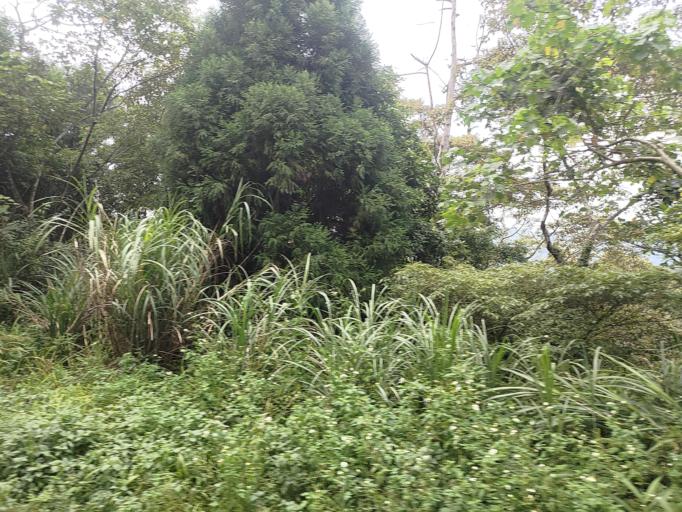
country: TW
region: Taiwan
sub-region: Hsinchu
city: Hsinchu
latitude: 24.6321
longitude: 121.0694
